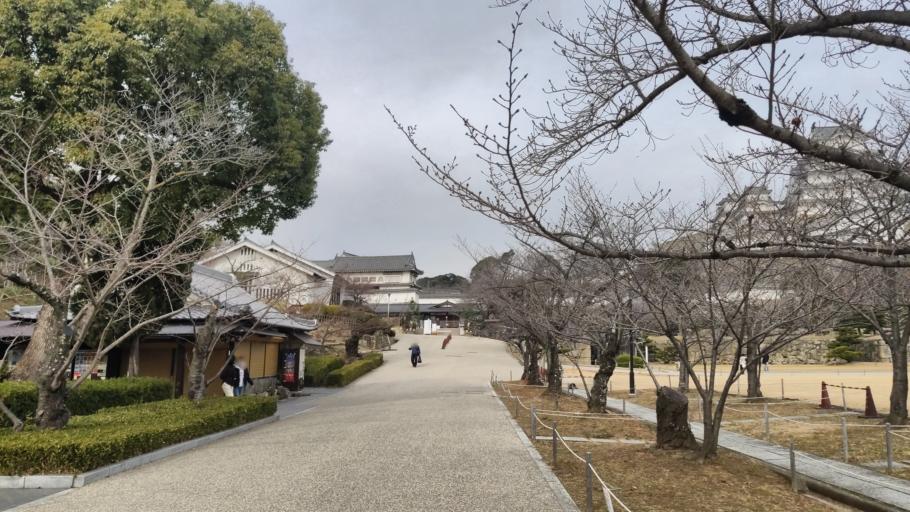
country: JP
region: Hyogo
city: Himeji
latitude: 34.8373
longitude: 134.6927
